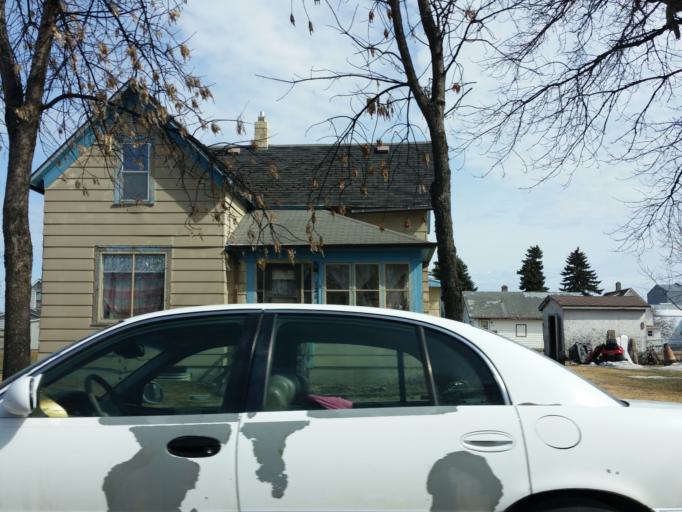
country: US
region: North Dakota
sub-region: Walsh County
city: Grafton
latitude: 48.4230
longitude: -97.4126
